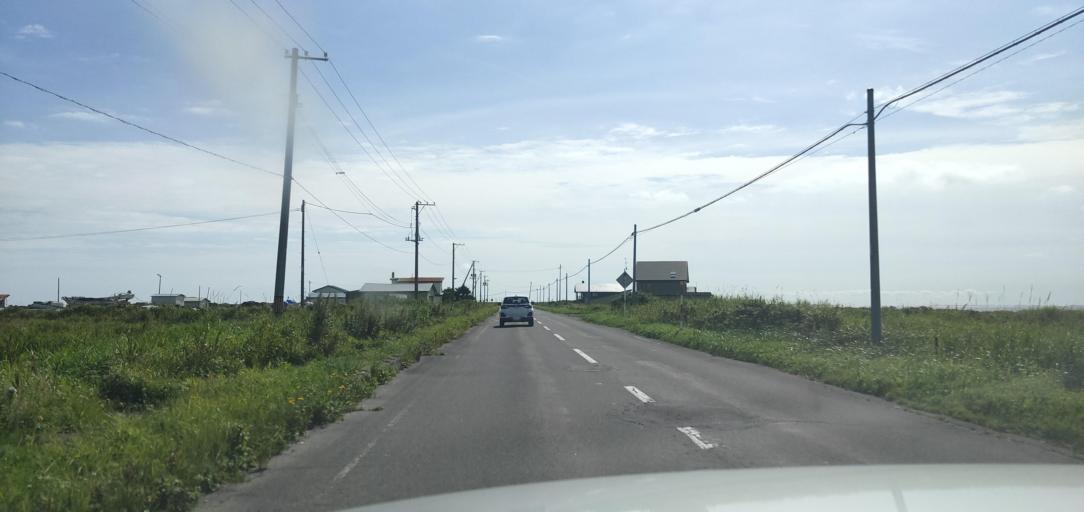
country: JP
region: Hokkaido
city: Shibetsu
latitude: 43.6294
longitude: 145.1924
